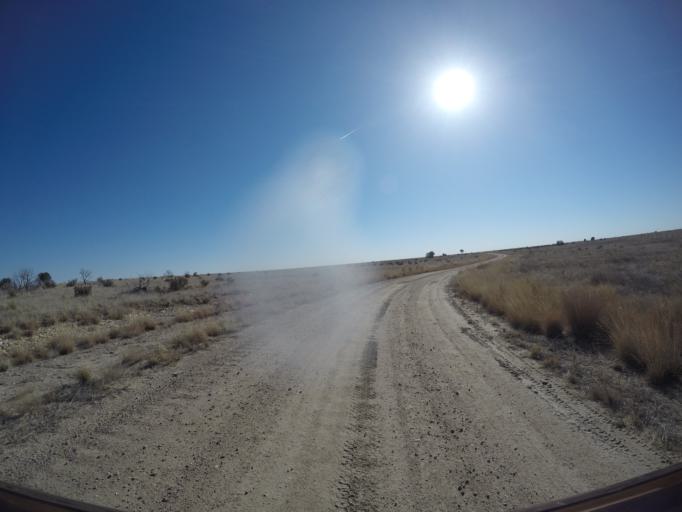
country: US
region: Colorado
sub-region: Otero County
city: La Junta
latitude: 37.6589
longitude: -103.6059
